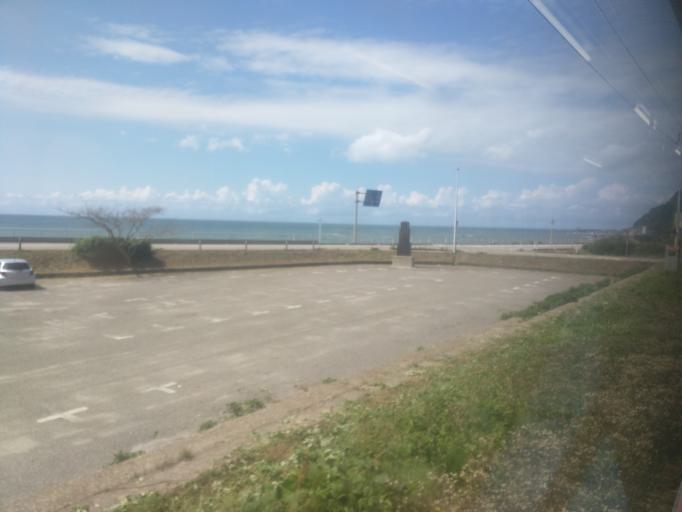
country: JP
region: Niigata
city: Murakami
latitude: 38.4536
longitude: 139.4956
